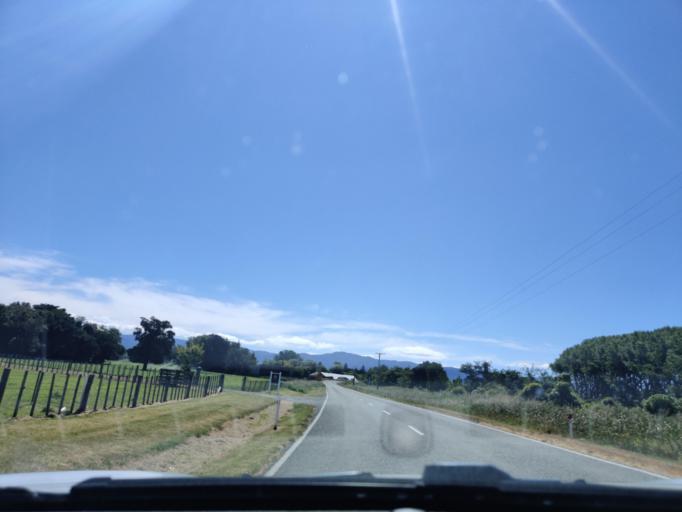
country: NZ
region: Wellington
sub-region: Upper Hutt City
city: Upper Hutt
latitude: -41.2888
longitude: 175.2710
